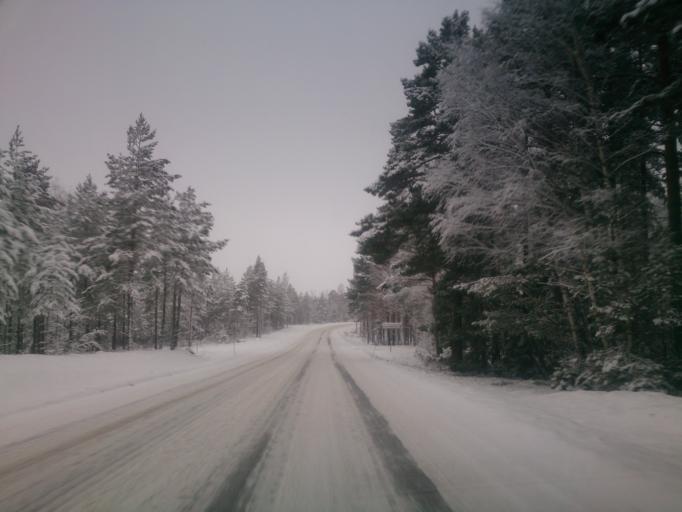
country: SE
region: OEstergoetland
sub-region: Finspangs Kommun
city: Finspang
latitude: 58.6645
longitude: 15.7725
